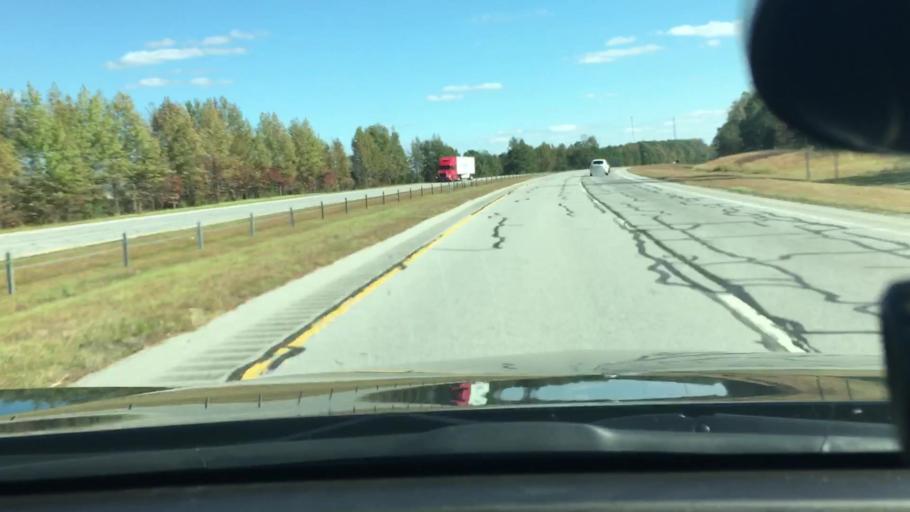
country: US
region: North Carolina
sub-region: Pitt County
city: Farmville
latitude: 35.6190
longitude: -77.5904
